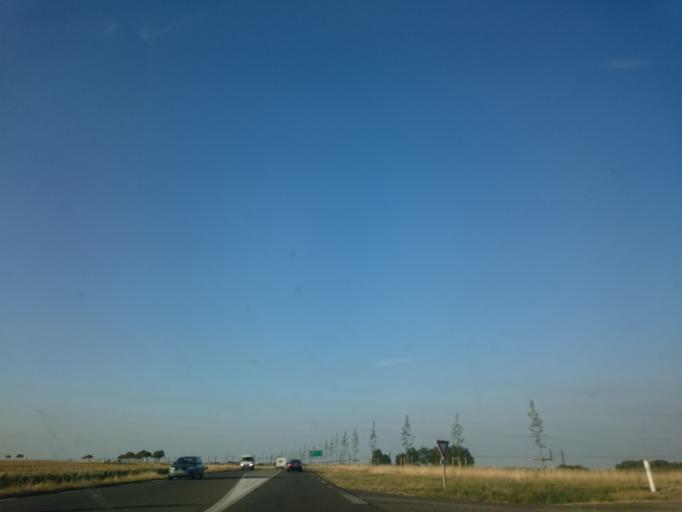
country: FR
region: Centre
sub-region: Departement d'Eure-et-Loir
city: Toury
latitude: 48.2067
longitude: 1.9437
